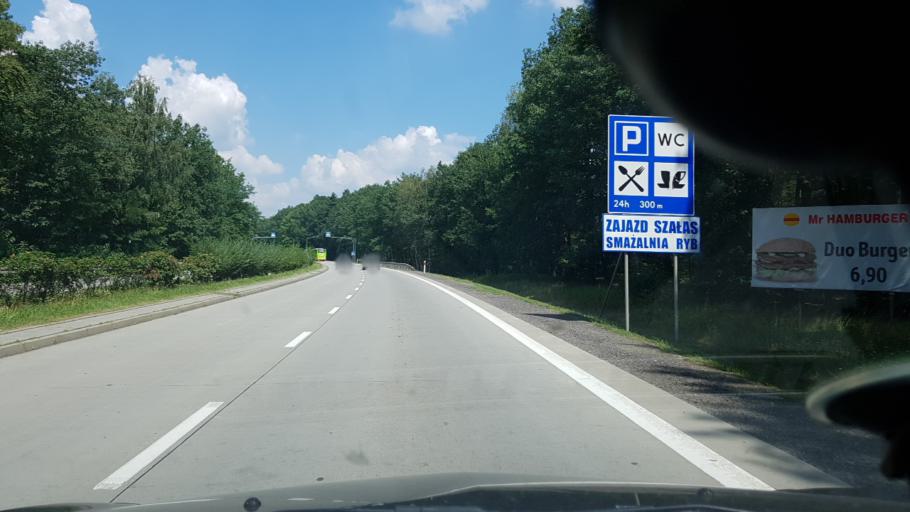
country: PL
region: Silesian Voivodeship
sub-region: Zory
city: Zory
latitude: 50.0546
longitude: 18.7208
